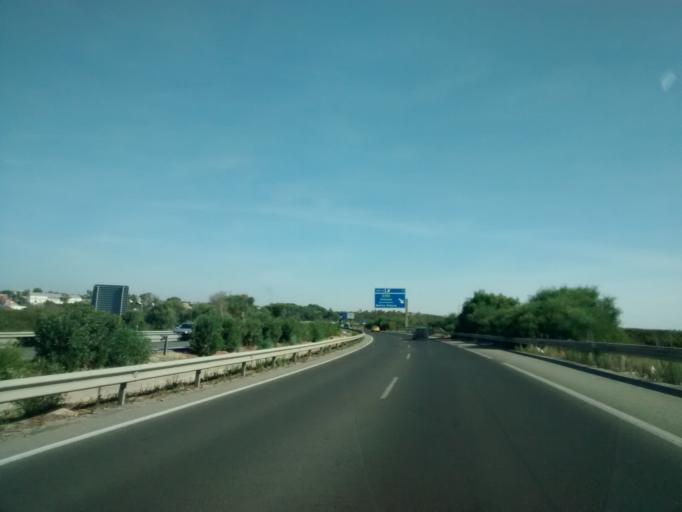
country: ES
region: Andalusia
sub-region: Provincia de Cadiz
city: Chiclana de la Frontera
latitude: 36.4105
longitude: -6.1192
